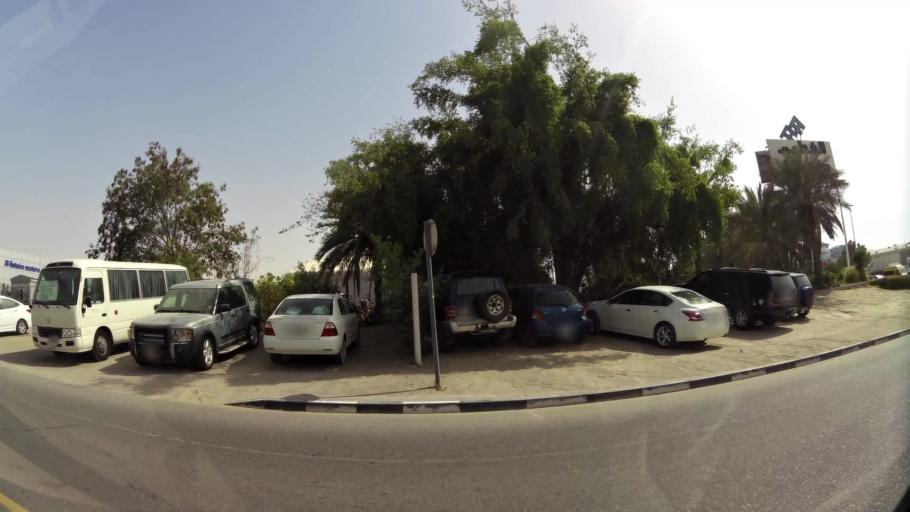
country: AE
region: Ash Shariqah
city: Sharjah
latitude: 25.2355
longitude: 55.3617
